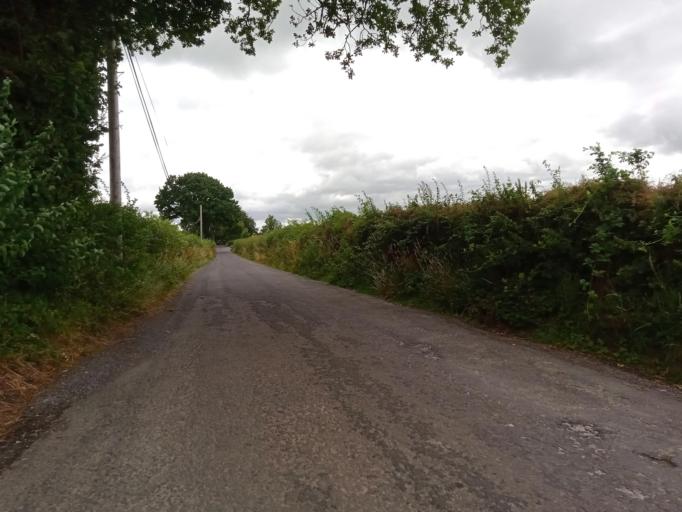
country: IE
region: Leinster
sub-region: Kilkenny
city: Callan
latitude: 52.5746
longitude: -7.3778
